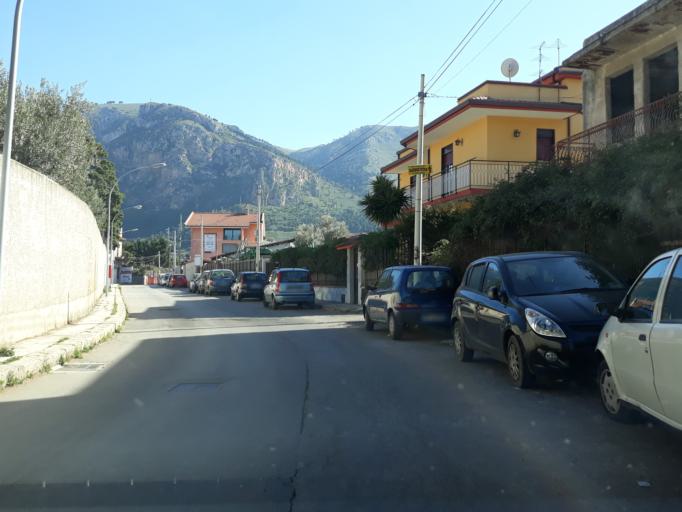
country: IT
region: Sicily
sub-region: Palermo
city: Villa Ciambra
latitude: 38.0853
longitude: 13.3448
